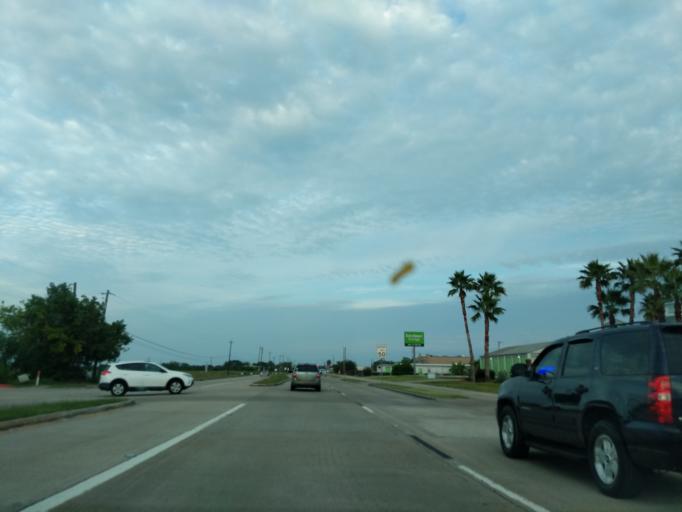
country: US
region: Texas
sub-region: Galveston County
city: Clear Lake Shores
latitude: 29.5286
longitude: -95.0378
